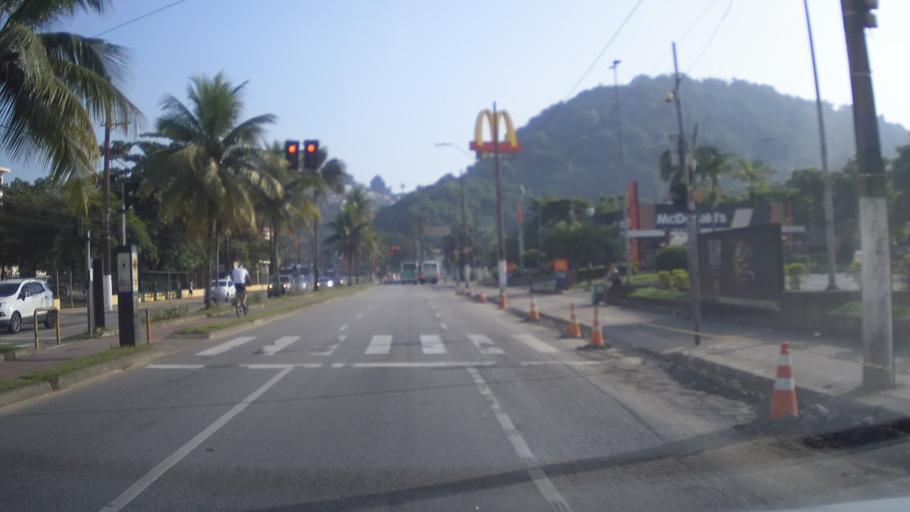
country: BR
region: Sao Paulo
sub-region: Santos
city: Santos
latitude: -23.9445
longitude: -46.3353
